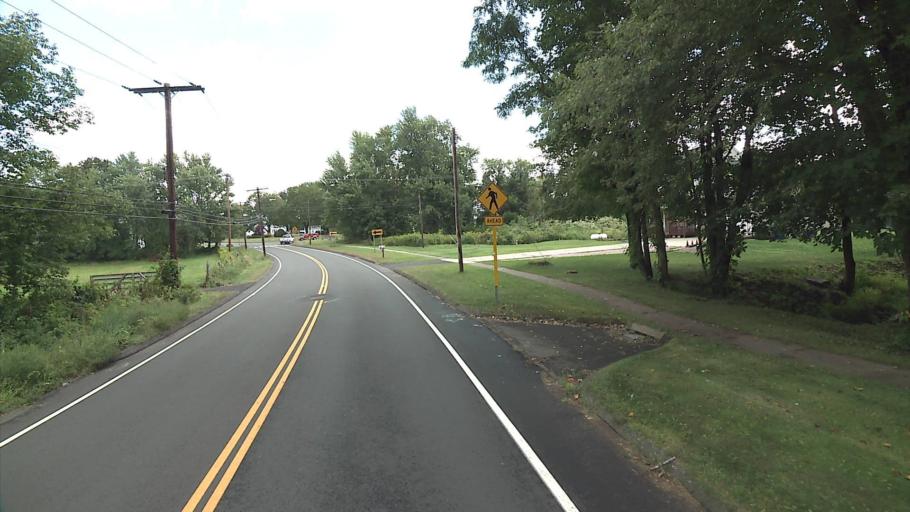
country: US
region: Connecticut
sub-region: Hartford County
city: Wethersfield
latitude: 41.6632
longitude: -72.6485
